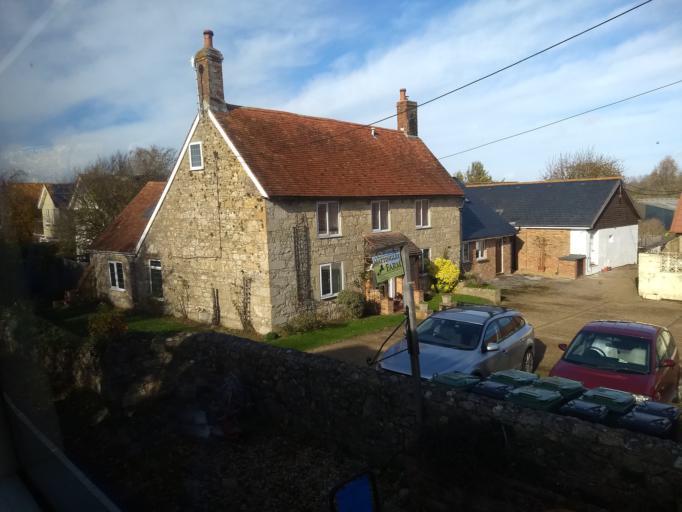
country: GB
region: England
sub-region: Isle of Wight
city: Shalfleet
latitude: 50.6920
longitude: -1.4554
